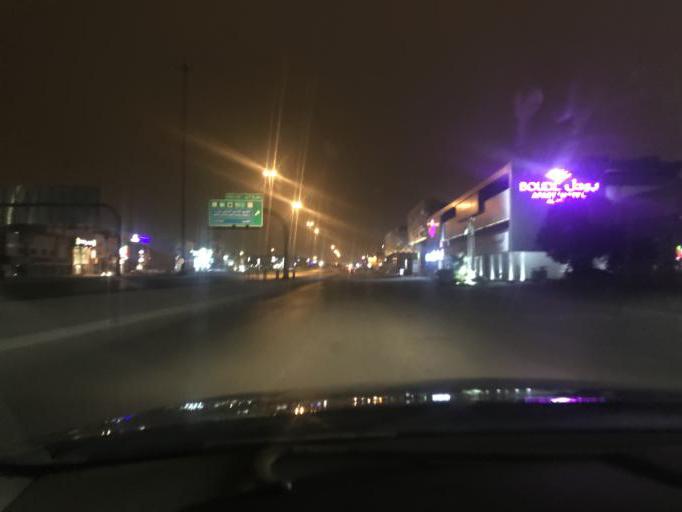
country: SA
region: Ar Riyad
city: Riyadh
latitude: 24.7972
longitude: 46.6979
